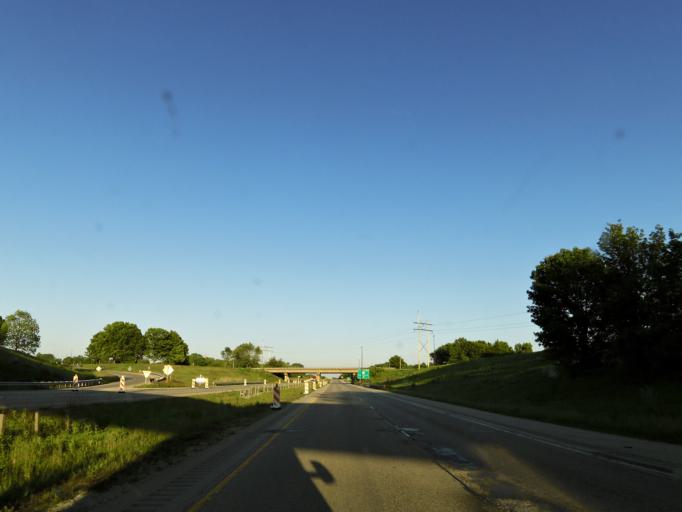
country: US
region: Illinois
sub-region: Vermilion County
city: Catlin
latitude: 40.1246
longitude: -87.7142
